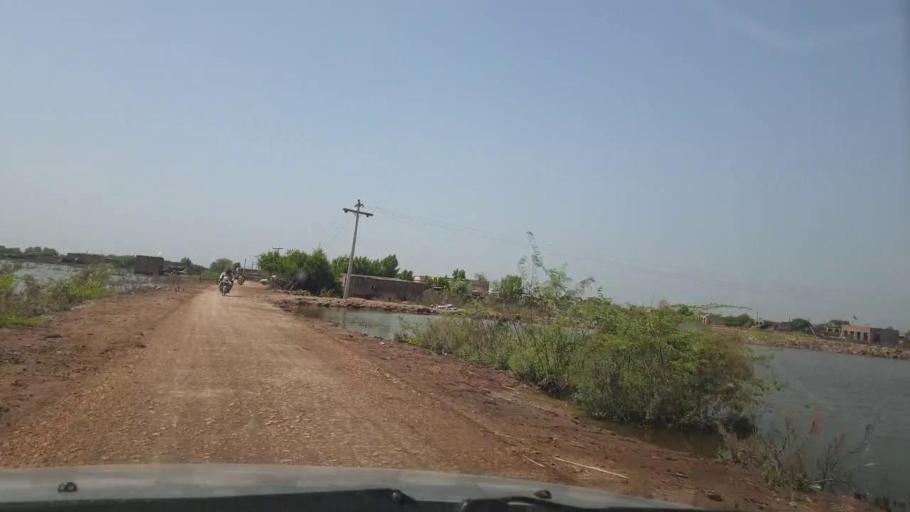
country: PK
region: Sindh
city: Tando Ghulam Ali
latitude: 25.1141
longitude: 68.7887
